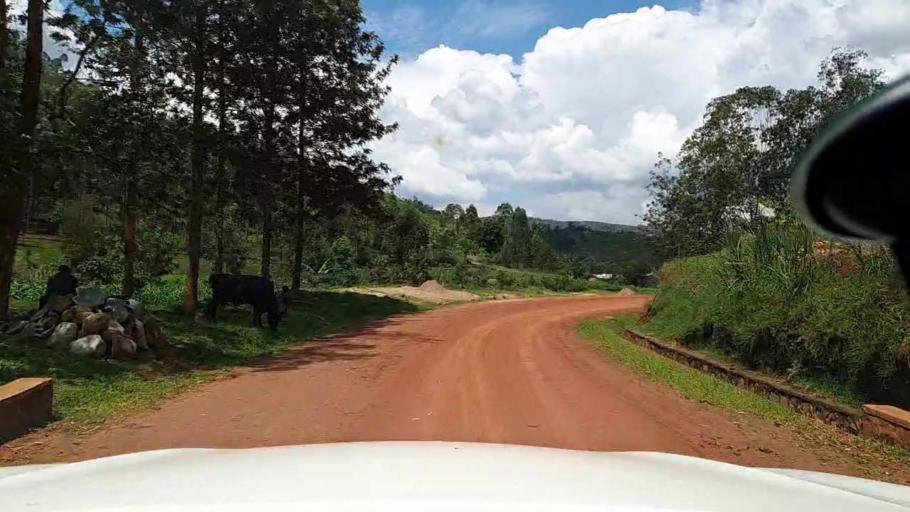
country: RW
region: Northern Province
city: Byumba
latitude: -1.6998
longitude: 29.8311
